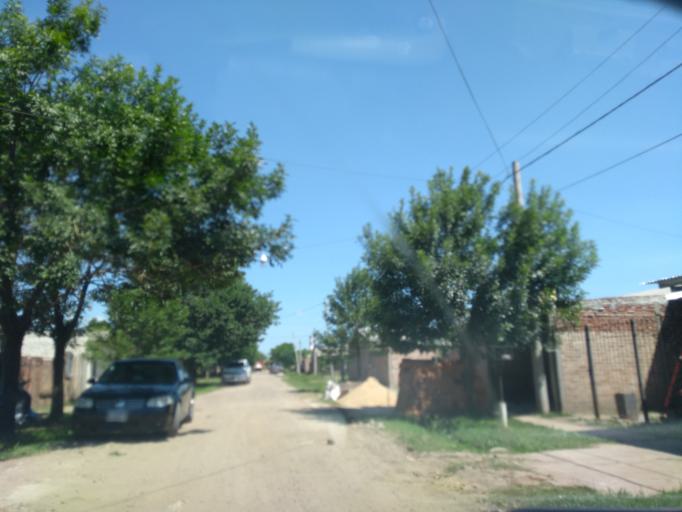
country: AR
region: Chaco
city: Fontana
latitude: -27.4132
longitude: -59.0375
